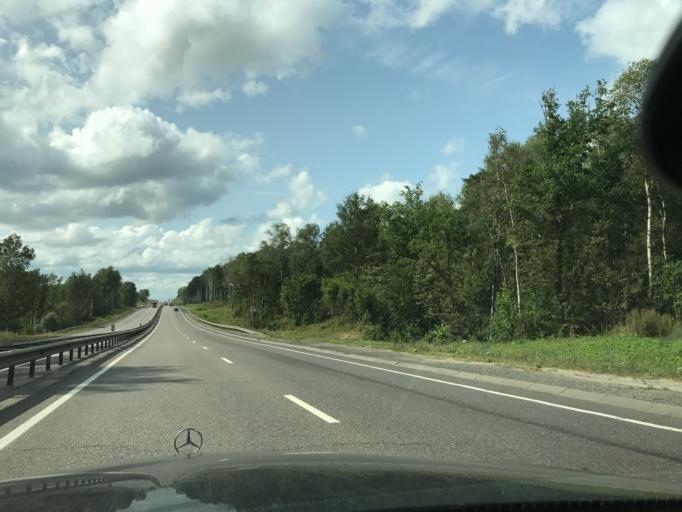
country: RU
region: Vladimir
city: Gorokhovets
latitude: 56.1605
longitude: 42.5815
